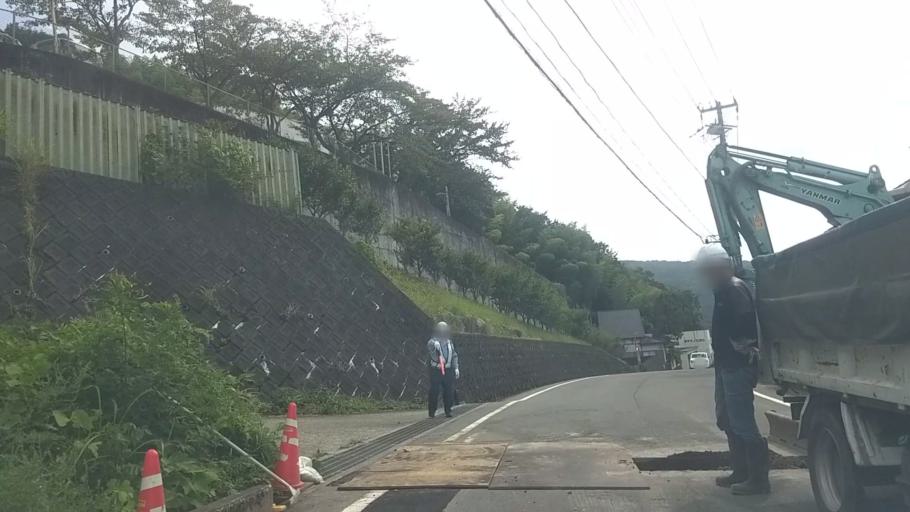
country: JP
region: Shizuoka
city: Ito
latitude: 34.9747
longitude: 138.9766
